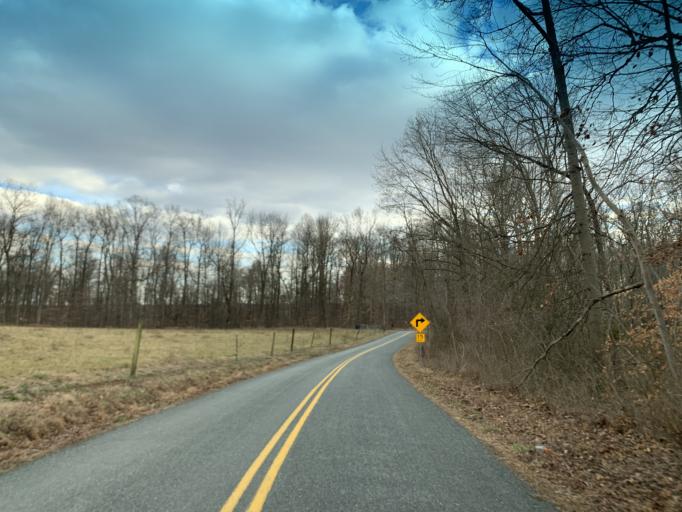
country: US
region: Maryland
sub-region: Harford County
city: South Bel Air
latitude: 39.5995
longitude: -76.2968
